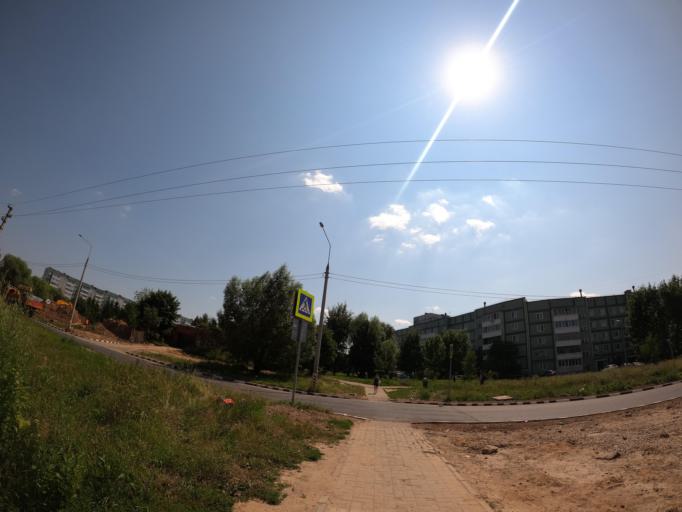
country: RU
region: Kaluga
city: Obninsk
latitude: 55.1227
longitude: 36.5884
